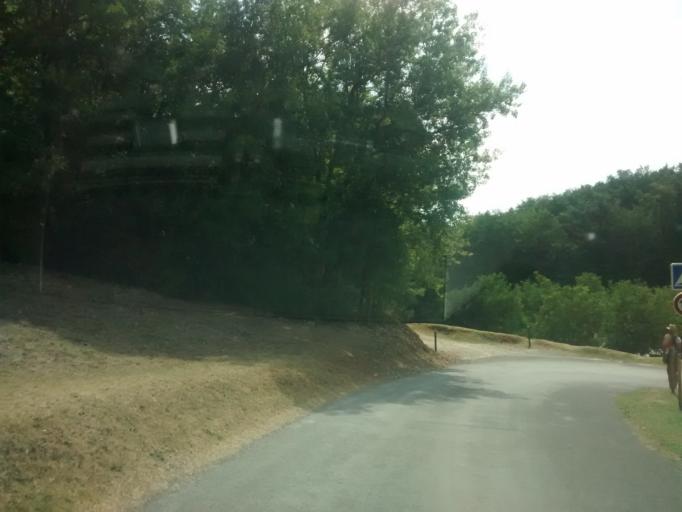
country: FR
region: Aquitaine
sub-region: Departement de la Dordogne
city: Cenac-et-Saint-Julien
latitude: 44.8162
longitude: 1.1441
